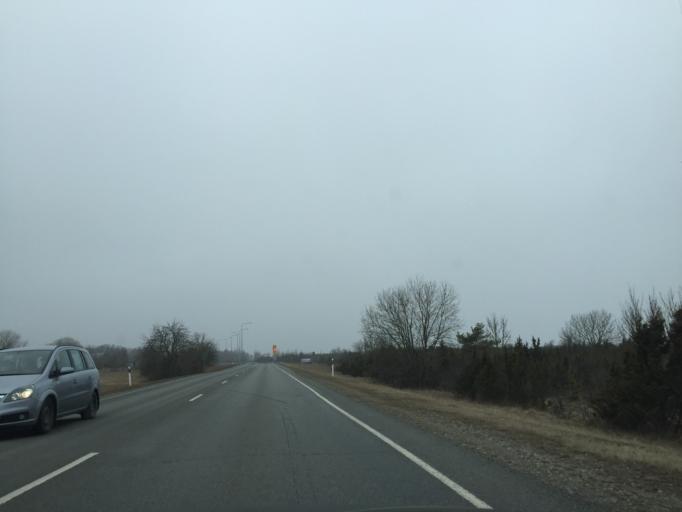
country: EE
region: Laeaene
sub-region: Lihula vald
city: Lihula
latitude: 58.5887
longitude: 23.5334
